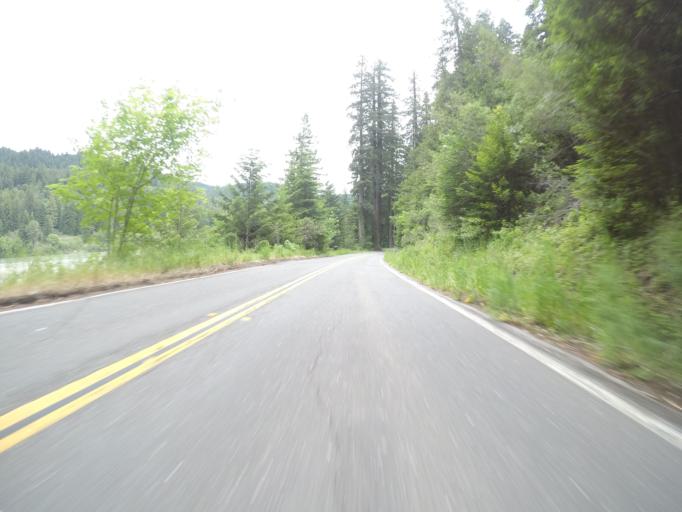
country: US
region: California
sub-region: Humboldt County
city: Rio Dell
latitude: 40.3911
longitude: -123.9302
